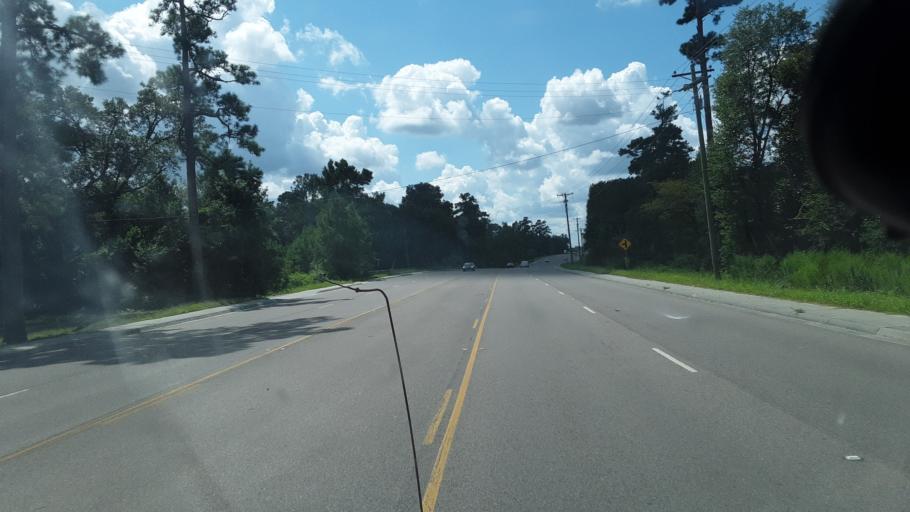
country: US
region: South Carolina
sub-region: Berkeley County
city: Moncks Corner
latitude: 33.1233
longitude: -80.0684
